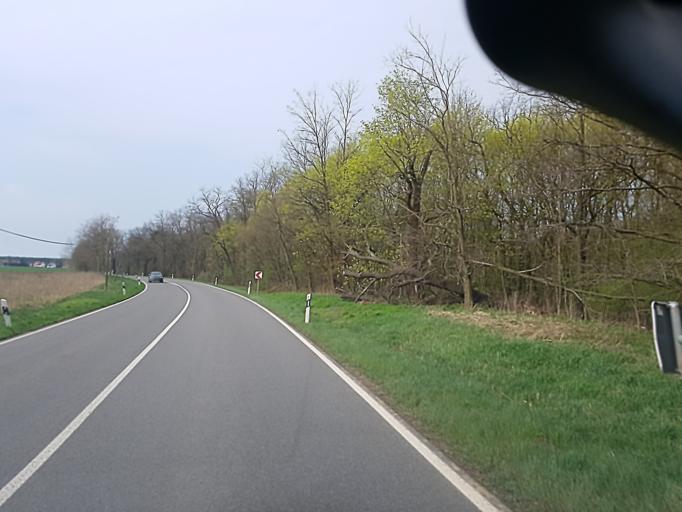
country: DE
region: Brandenburg
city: Falkenberg
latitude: 51.5450
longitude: 13.2368
